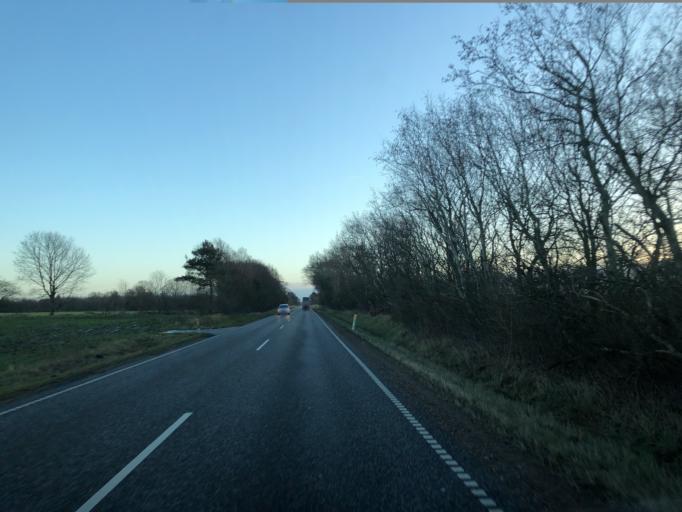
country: DK
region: Central Jutland
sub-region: Skive Kommune
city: Skive
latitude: 56.4794
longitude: 8.9580
